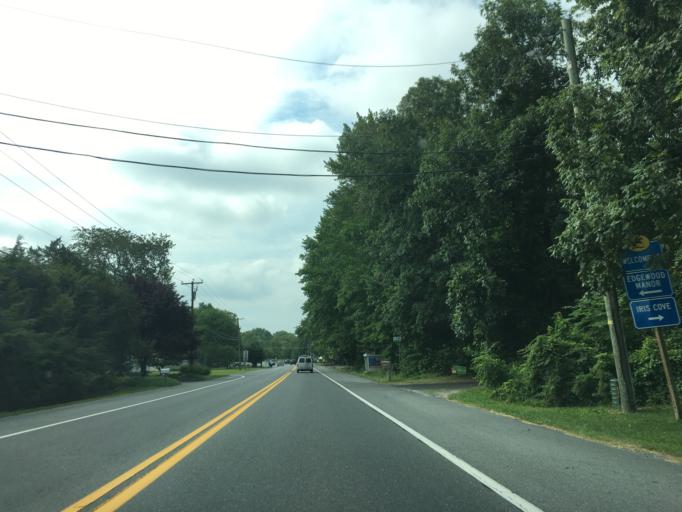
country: US
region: Delaware
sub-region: Sussex County
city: Ocean View
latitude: 38.5527
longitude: -75.1517
